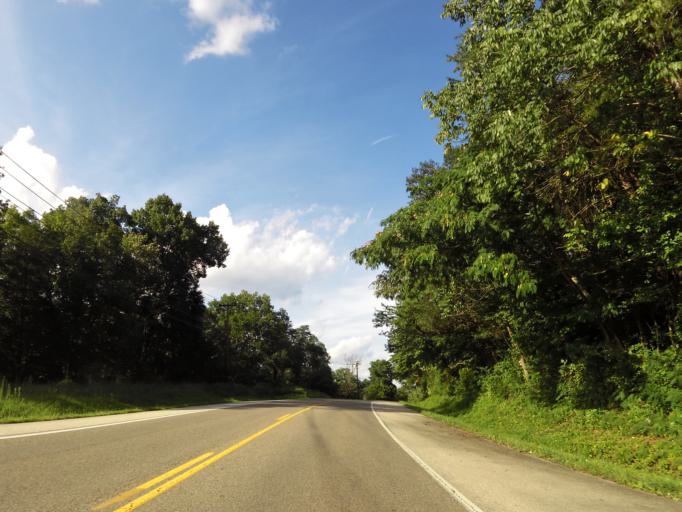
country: US
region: Tennessee
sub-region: Blount County
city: Louisville
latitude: 35.8394
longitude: -84.0065
